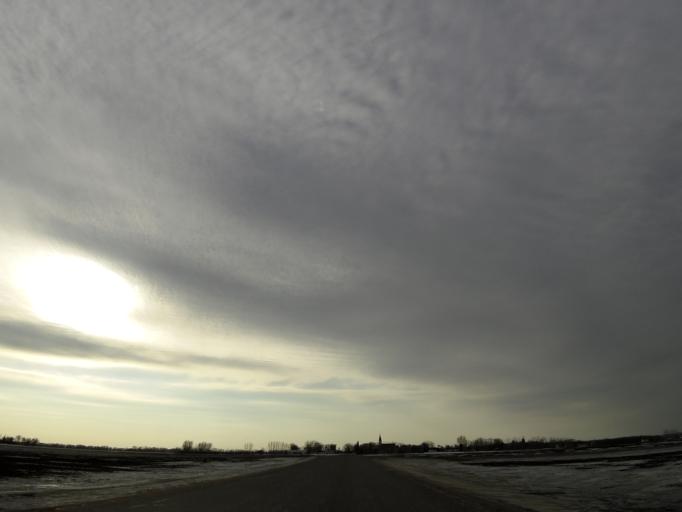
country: US
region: North Dakota
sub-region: Walsh County
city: Grafton
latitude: 48.4267
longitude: -97.2839
